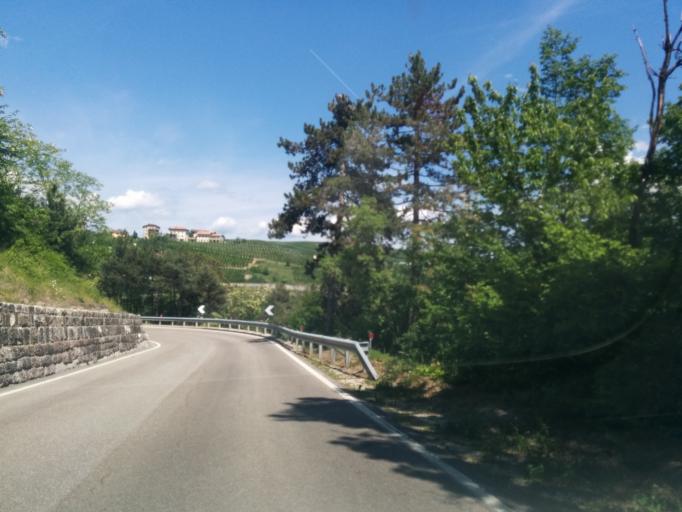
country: IT
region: Trentino-Alto Adige
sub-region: Provincia di Trento
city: Terres
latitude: 46.3147
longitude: 11.0203
